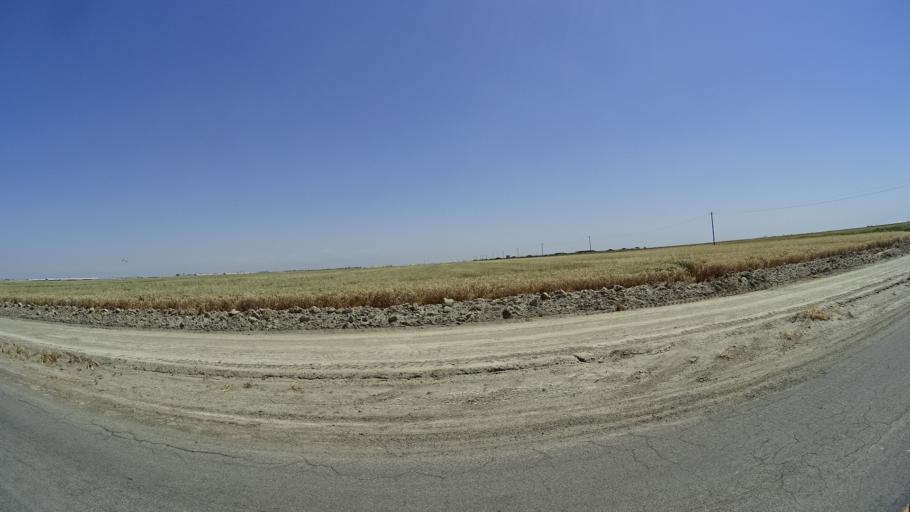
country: US
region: California
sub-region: Kings County
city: Stratford
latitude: 36.1901
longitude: -119.7085
